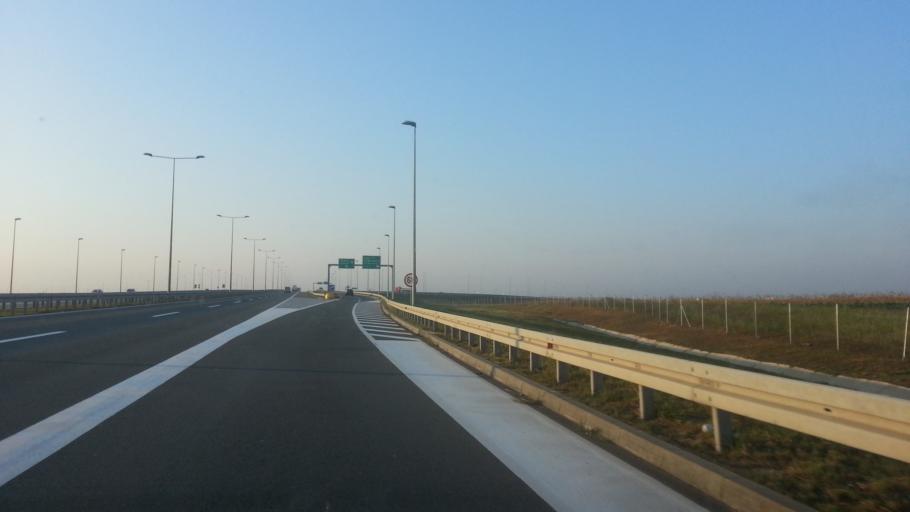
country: RS
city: Dobanovci
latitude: 44.8416
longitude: 20.2500
